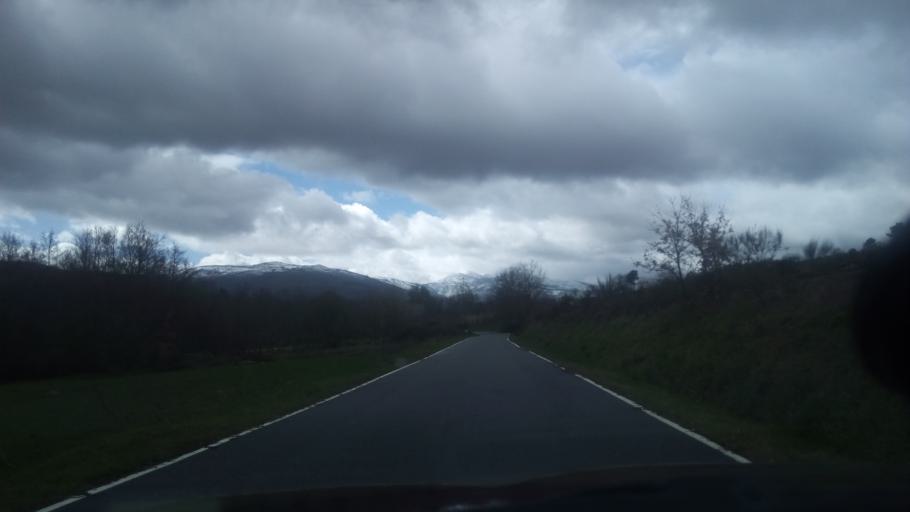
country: PT
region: Guarda
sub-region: Fornos de Algodres
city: Fornos de Algodres
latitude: 40.5707
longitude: -7.4693
